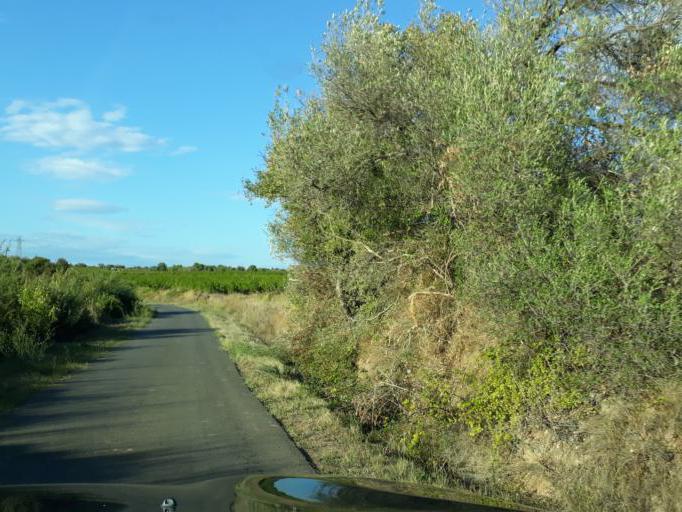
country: FR
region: Languedoc-Roussillon
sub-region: Departement de l'Herault
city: Florensac
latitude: 43.4078
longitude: 3.4759
